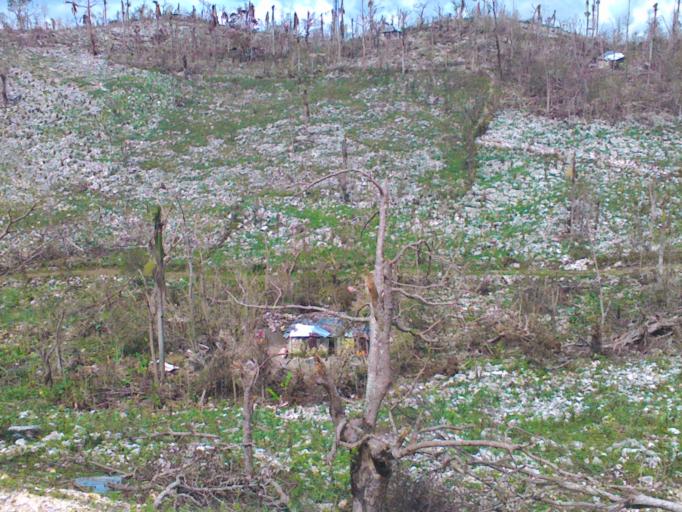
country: HT
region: Grandans
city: Jeremie
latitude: 18.5006
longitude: -74.0943
